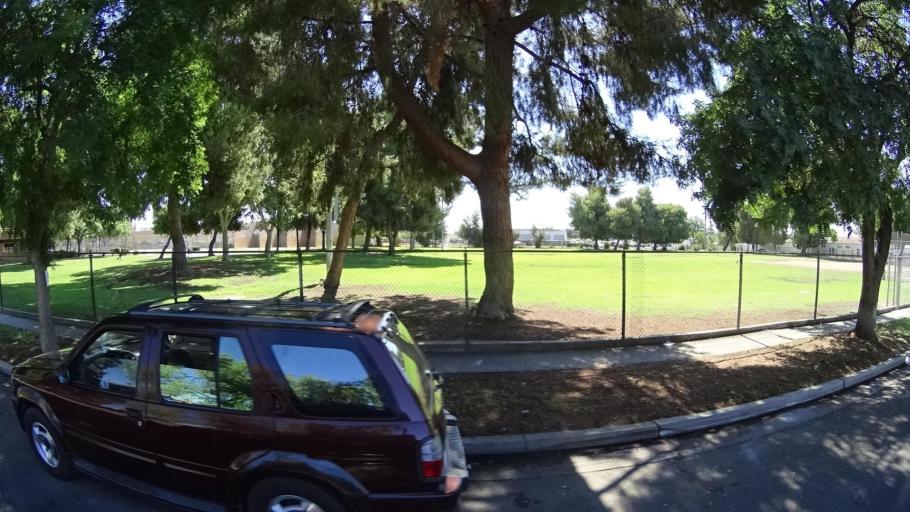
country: US
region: California
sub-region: Fresno County
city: Fresno
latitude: 36.7748
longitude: -119.7928
